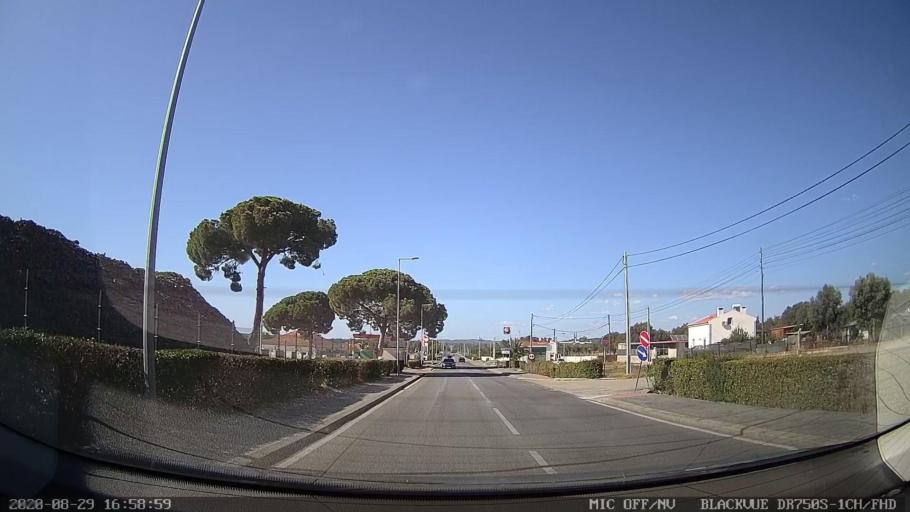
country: PT
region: Setubal
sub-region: Alcacer do Sal
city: Alcacer do Sal
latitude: 38.3912
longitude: -8.5136
